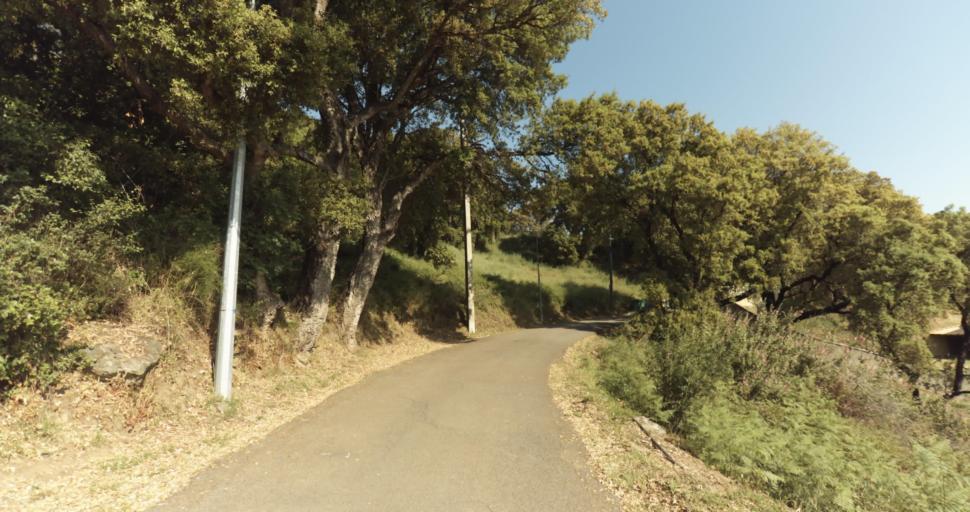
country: FR
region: Corsica
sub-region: Departement de la Haute-Corse
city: Biguglia
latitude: 42.6304
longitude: 9.4178
